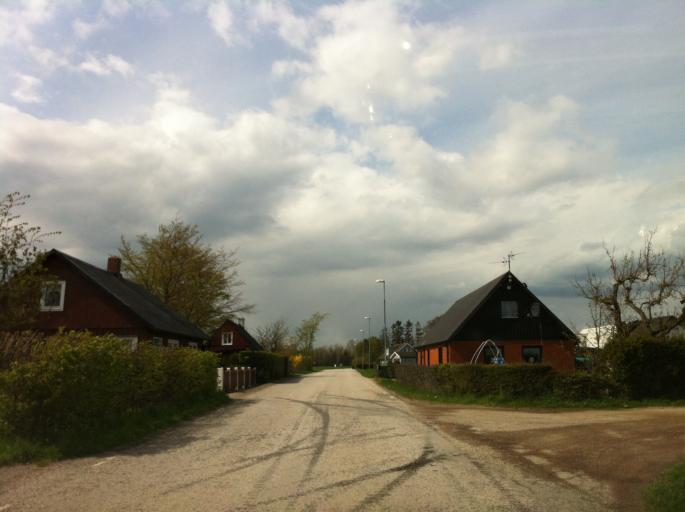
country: SE
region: Skane
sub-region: Kavlinge Kommun
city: Kaevlinge
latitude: 55.8087
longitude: 13.1485
